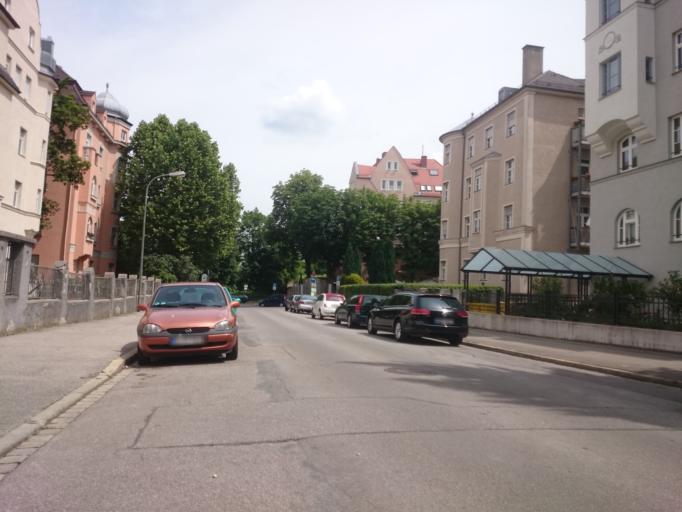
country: DE
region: Bavaria
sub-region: Swabia
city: Augsburg
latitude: 48.3786
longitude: 10.8911
